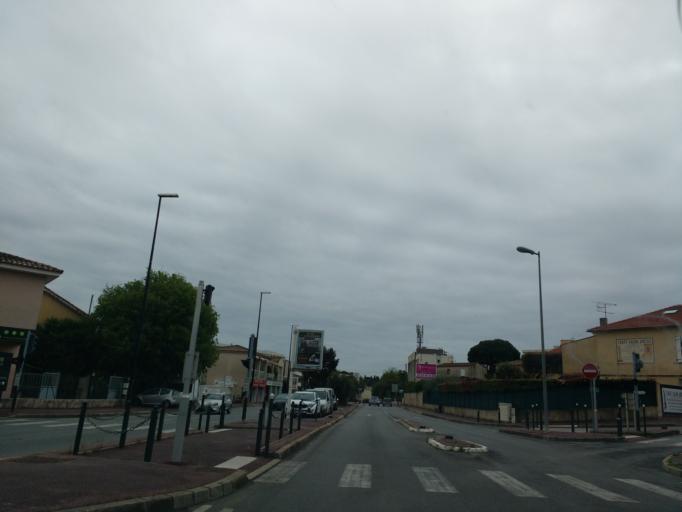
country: FR
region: Provence-Alpes-Cote d'Azur
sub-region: Departement des Alpes-Maritimes
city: Le Cannet
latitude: 43.5688
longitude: 7.0022
